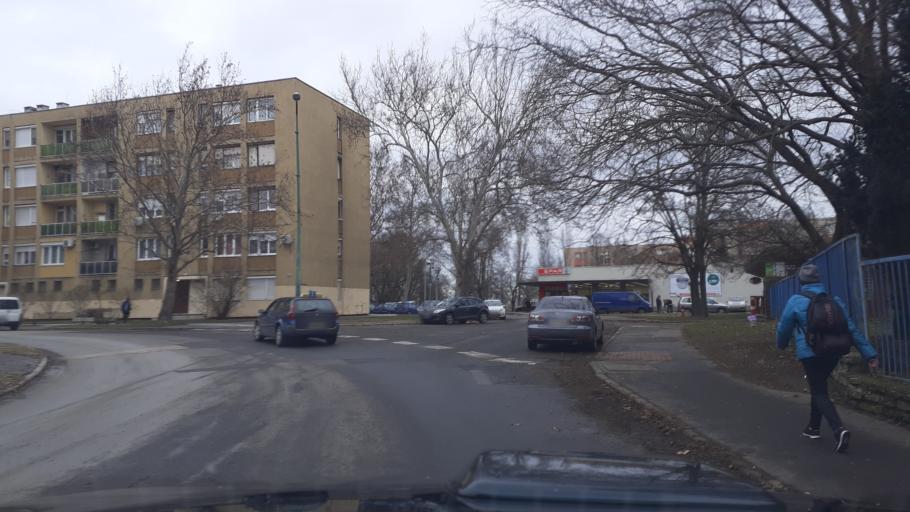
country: HU
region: Fejer
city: dunaujvaros
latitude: 46.9703
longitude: 18.9373
